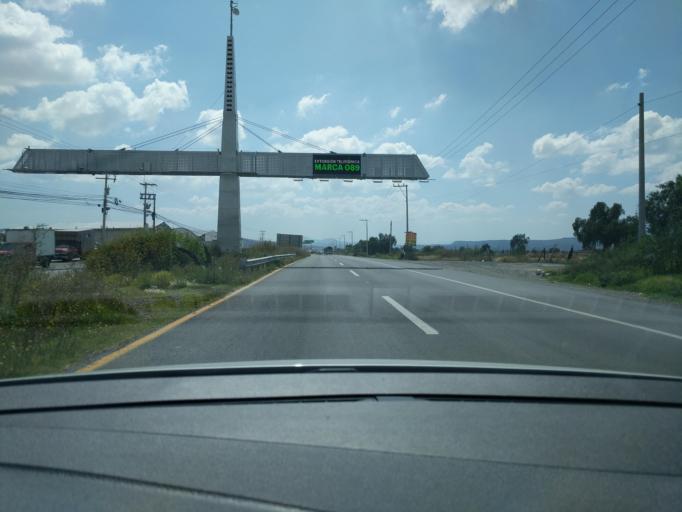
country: MX
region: Hidalgo
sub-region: Mineral de la Reforma
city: Rinconada de los Angeles
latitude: 20.0321
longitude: -98.7287
